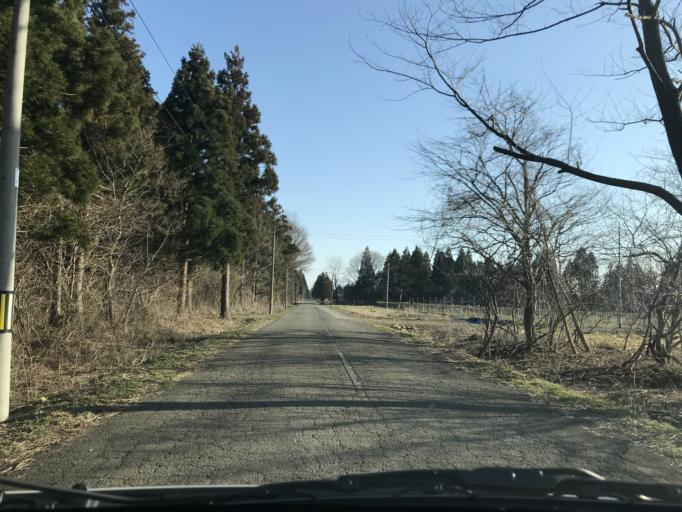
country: JP
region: Iwate
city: Kitakami
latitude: 39.2486
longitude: 141.0399
